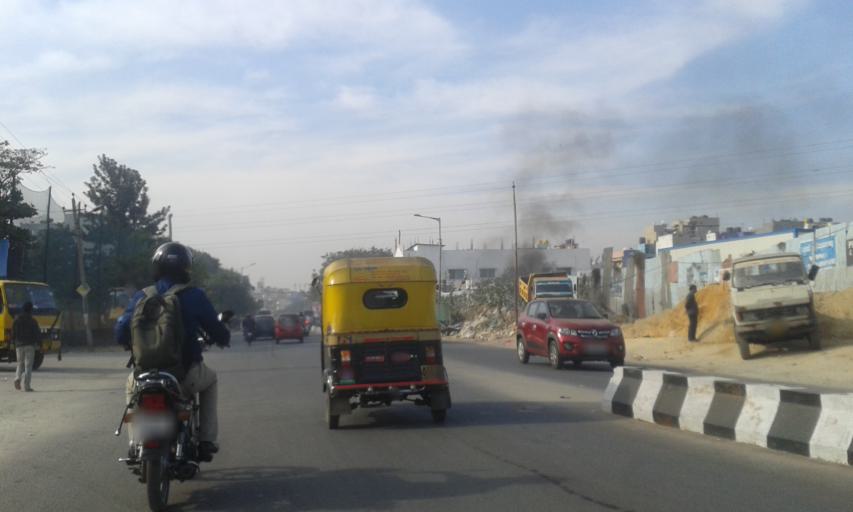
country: IN
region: Karnataka
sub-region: Bangalore Urban
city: Bangalore
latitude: 12.9500
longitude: 77.6208
